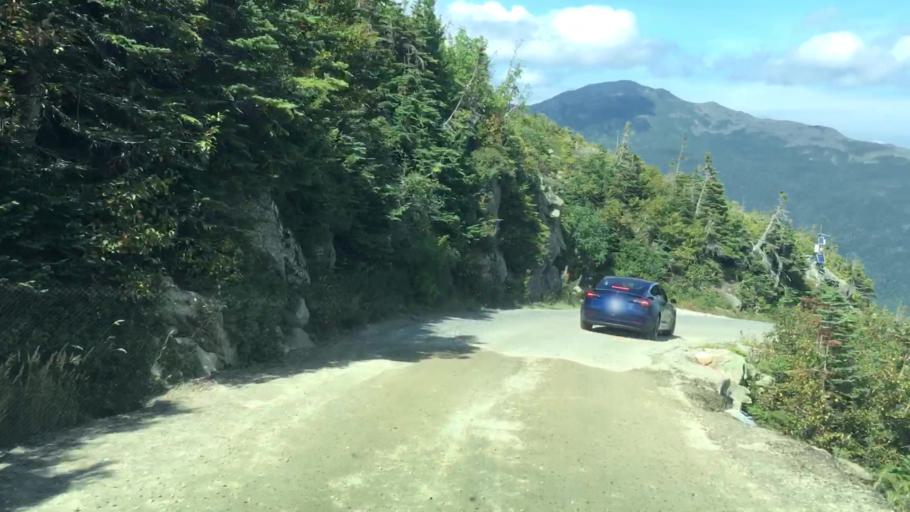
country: US
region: New Hampshire
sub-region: Coos County
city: Gorham
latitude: 44.2890
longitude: -71.2800
